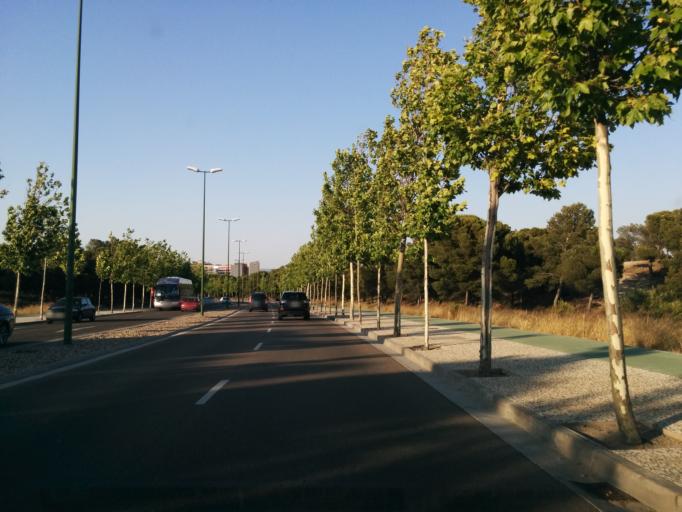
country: ES
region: Aragon
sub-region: Provincia de Zaragoza
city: Zaragoza
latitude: 41.6103
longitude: -0.8785
